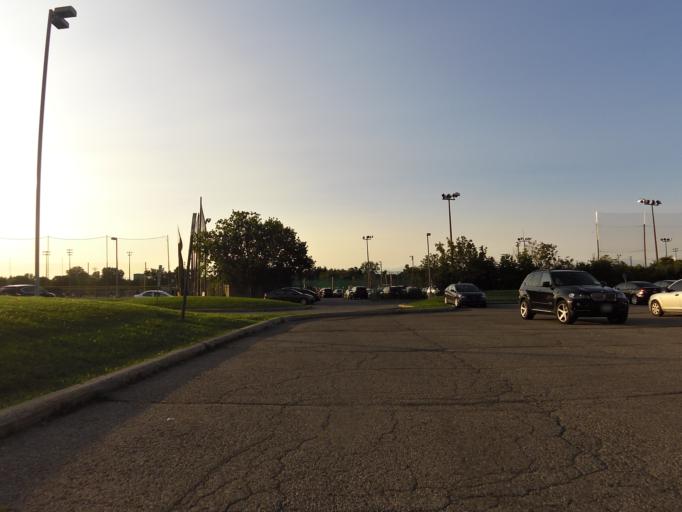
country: CA
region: Ontario
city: Ottawa
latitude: 45.3828
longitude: -75.6813
